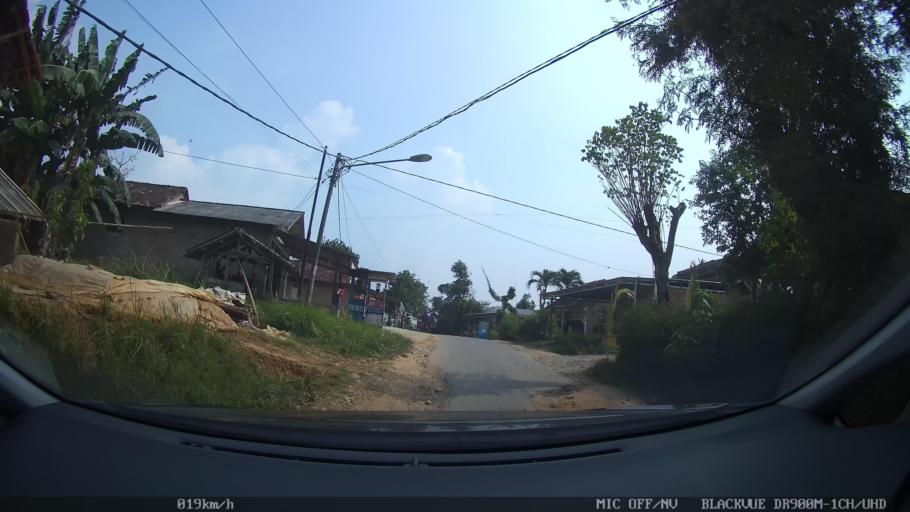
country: ID
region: Lampung
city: Pringsewu
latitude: -5.3946
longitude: 104.9923
